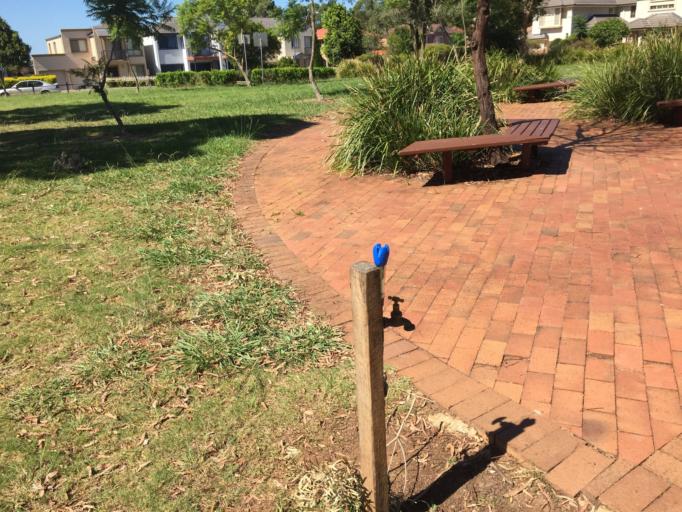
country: AU
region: New South Wales
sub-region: Blacktown
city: Stanhope Gardens
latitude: -33.7269
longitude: 150.9087
